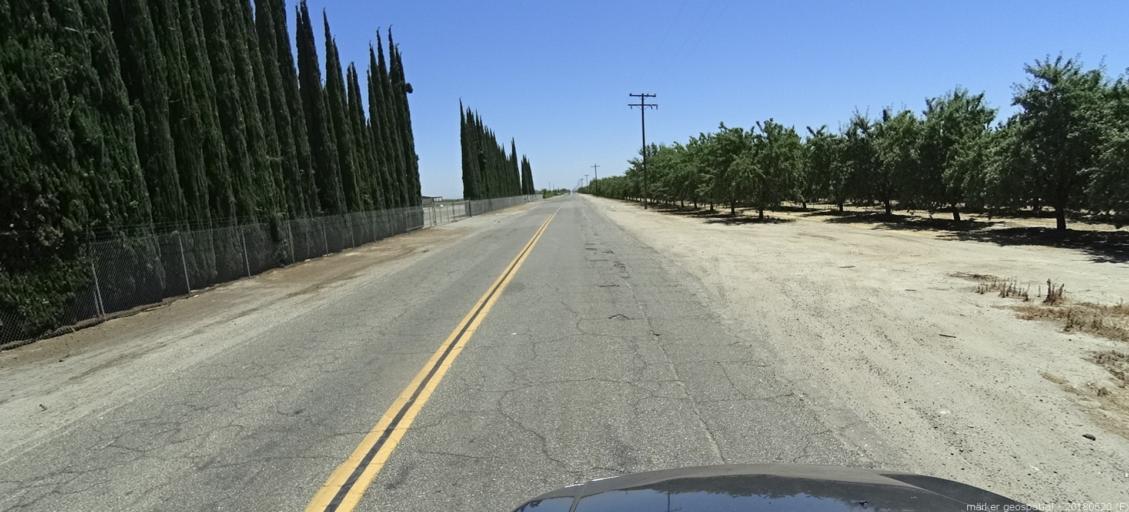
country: US
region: California
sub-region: Madera County
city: Parkwood
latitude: 36.8659
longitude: -120.0552
